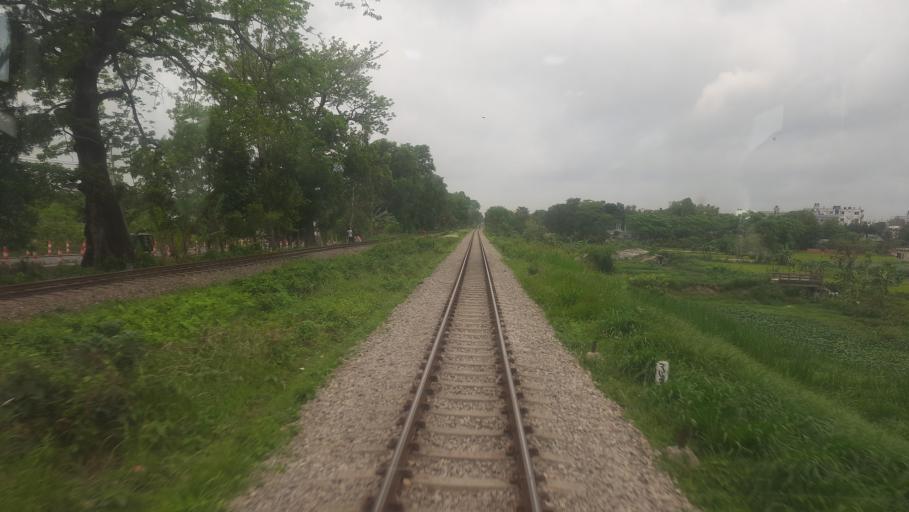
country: BD
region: Dhaka
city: Narsingdi
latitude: 23.9317
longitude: 90.7360
